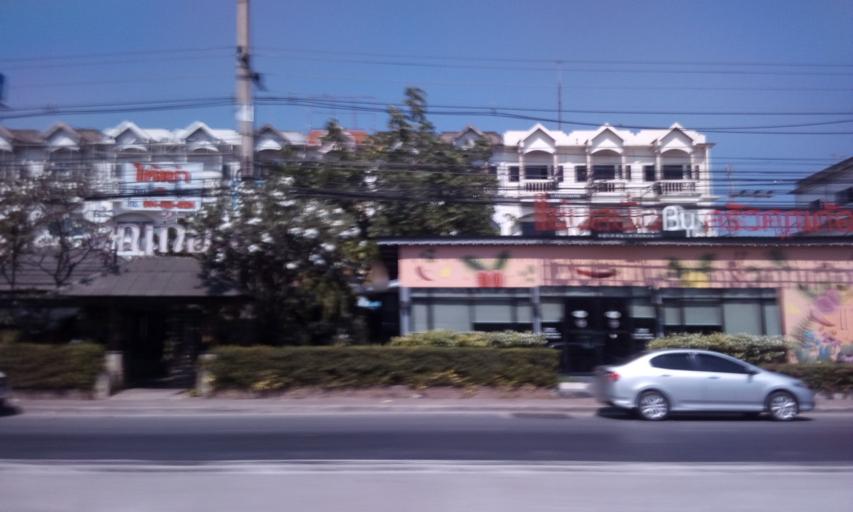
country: TH
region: Pathum Thani
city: Ban Rangsit
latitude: 14.0554
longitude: 100.8294
